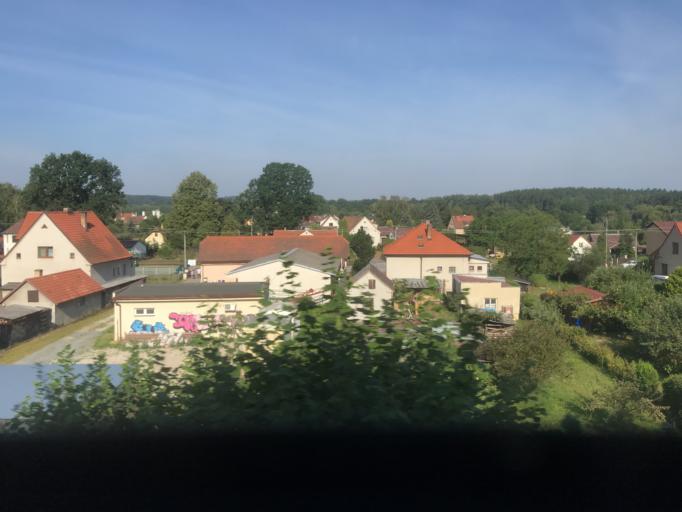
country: CZ
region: Jihocesky
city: Sobeslav
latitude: 49.3031
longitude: 14.7198
